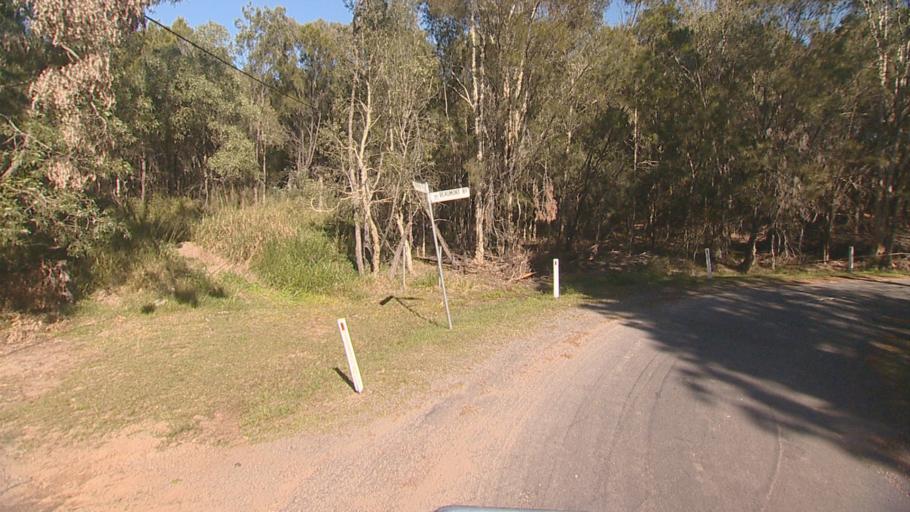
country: AU
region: Queensland
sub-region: Logan
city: Logan Reserve
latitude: -27.7156
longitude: 153.0766
